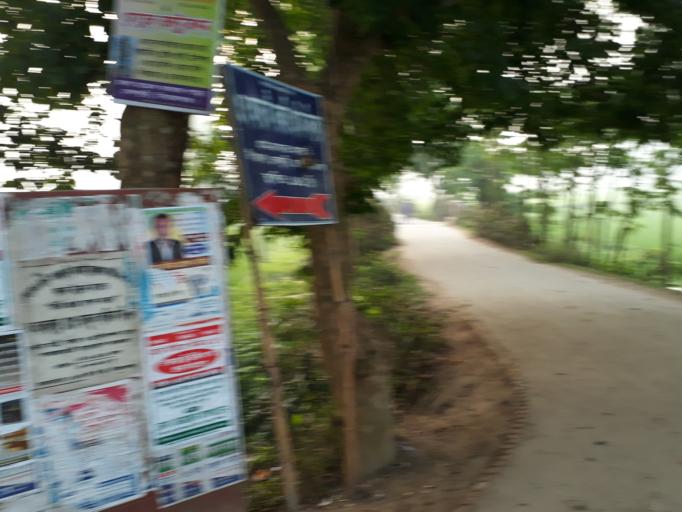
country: BD
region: Rajshahi
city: Sirajganj
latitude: 24.3224
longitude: 89.6743
